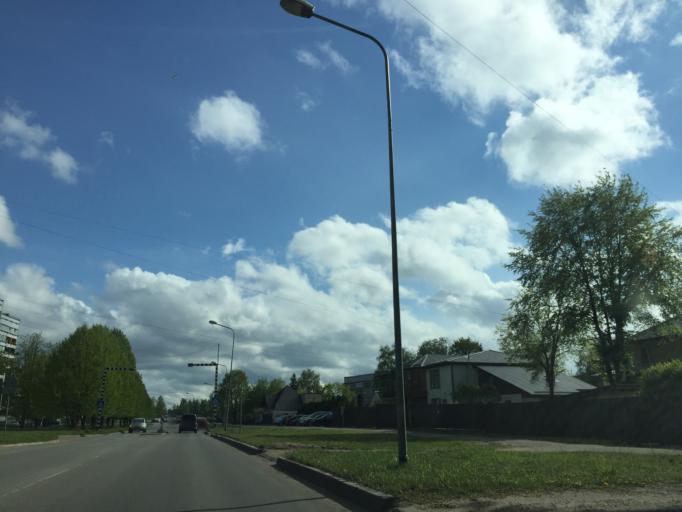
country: LV
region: Riga
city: Riga
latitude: 56.9352
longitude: 24.1952
